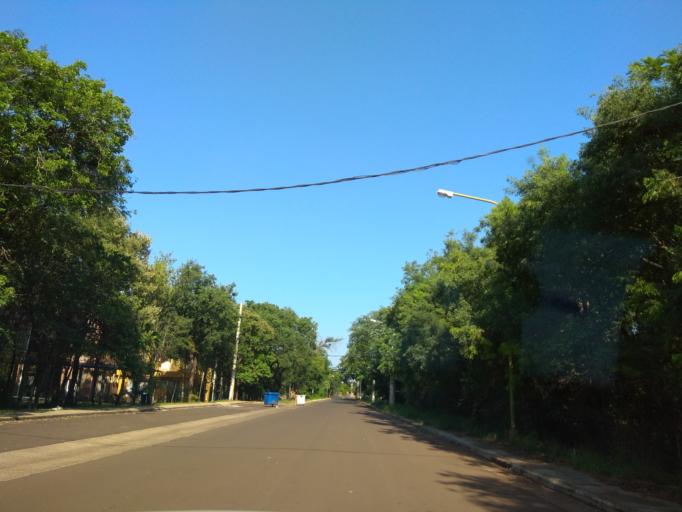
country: AR
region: Misiones
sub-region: Departamento de Capital
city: Posadas
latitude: -27.3562
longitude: -55.9403
